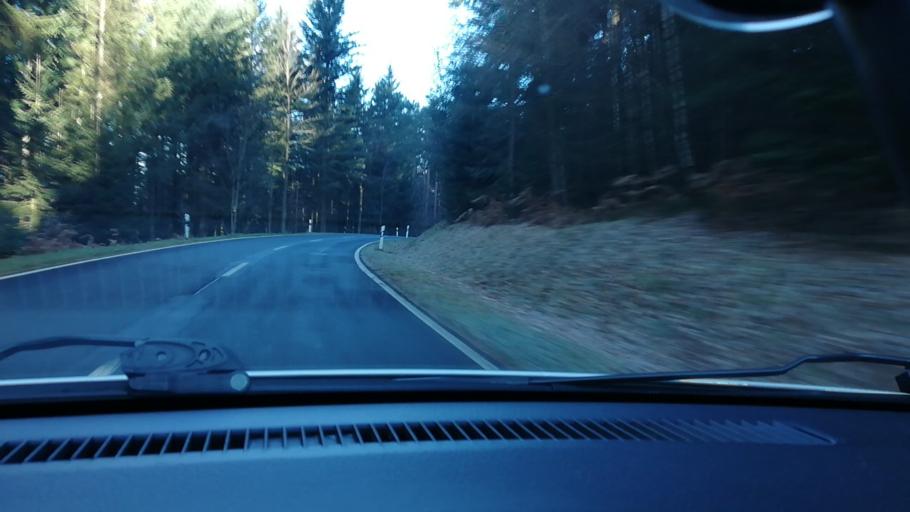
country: DE
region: Bavaria
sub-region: Regierungsbezirk Unterfranken
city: Heigenbrucken
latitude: 50.0015
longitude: 9.3672
